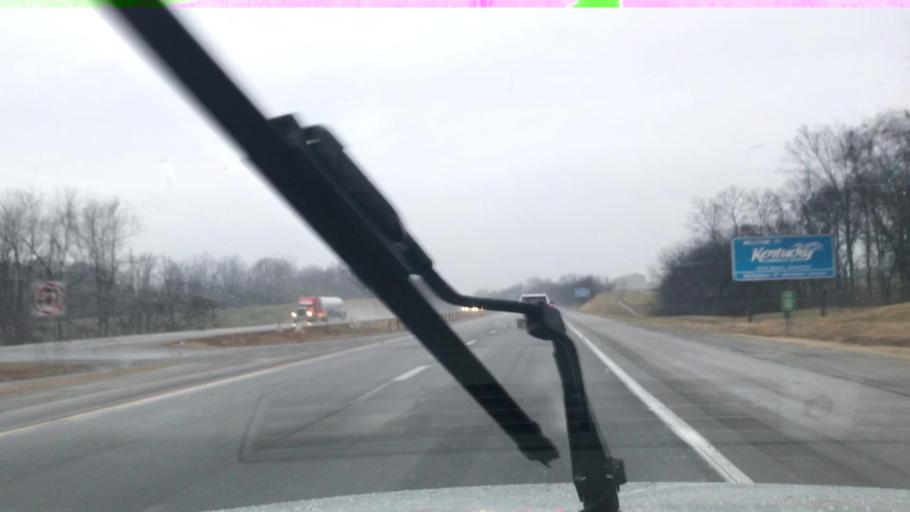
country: US
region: Kentucky
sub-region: Christian County
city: Oak Grove
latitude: 36.6418
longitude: -87.3395
